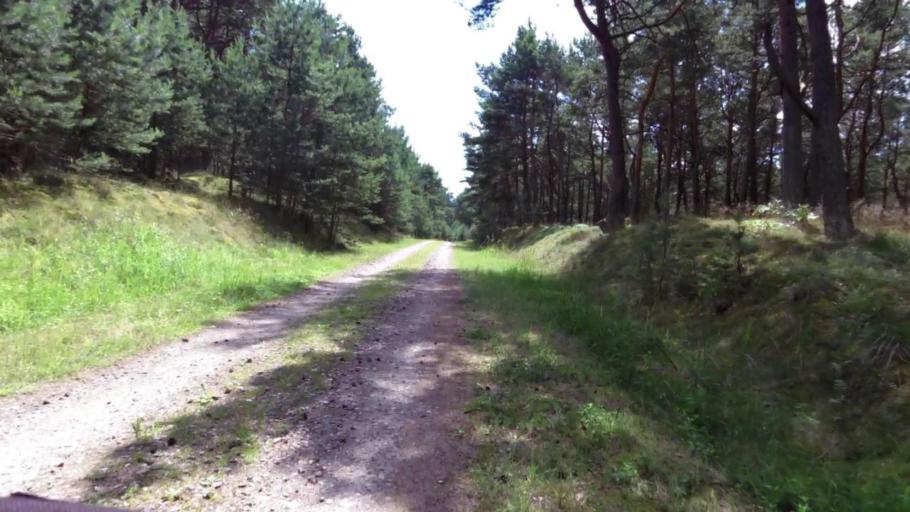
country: PL
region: West Pomeranian Voivodeship
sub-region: Powiat gryficki
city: Mrzezyno
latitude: 54.1264
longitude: 15.2207
